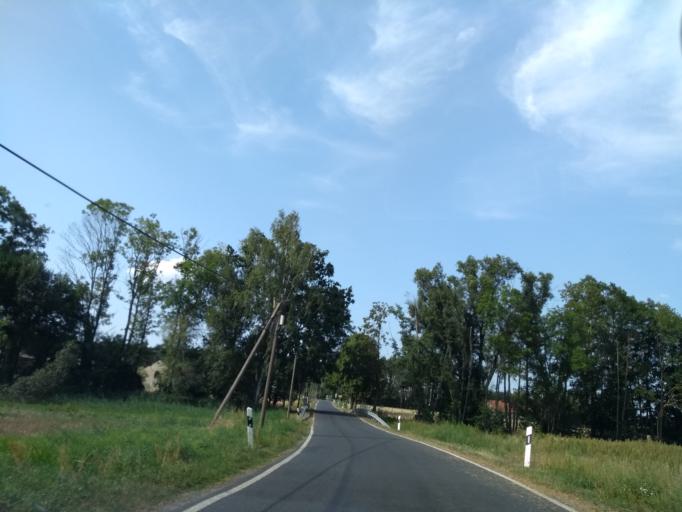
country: DE
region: Brandenburg
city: Luebben
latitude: 51.8639
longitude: 13.8524
